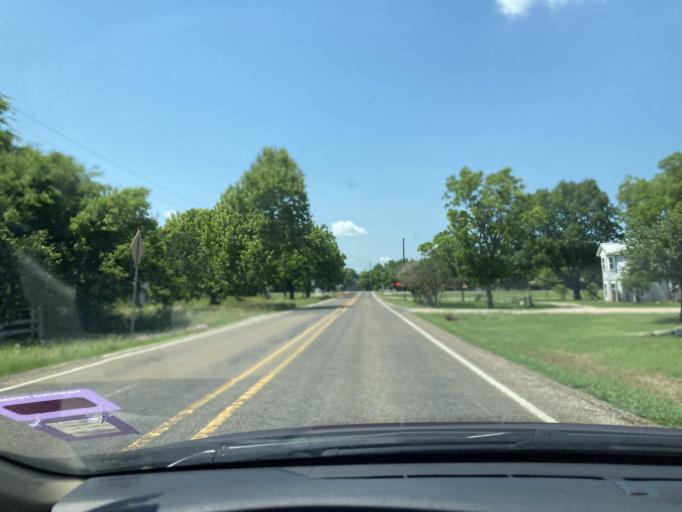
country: US
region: Texas
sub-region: Navarro County
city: Kerens
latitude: 32.1158
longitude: -96.3278
